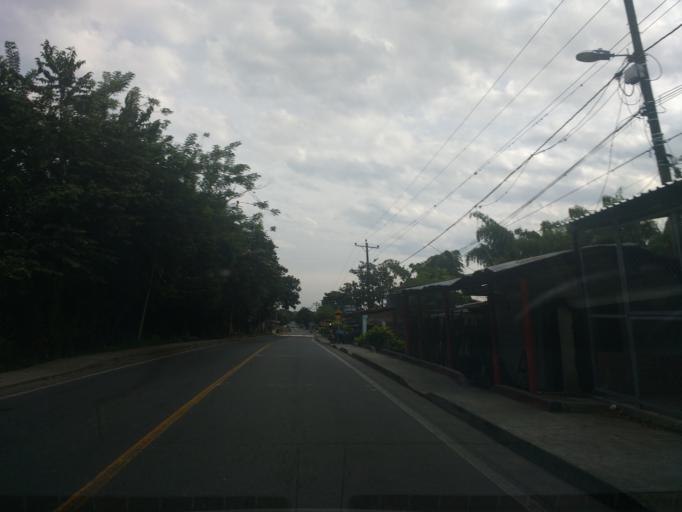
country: CO
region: Cauca
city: Miranda
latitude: 3.2819
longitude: -76.2235
